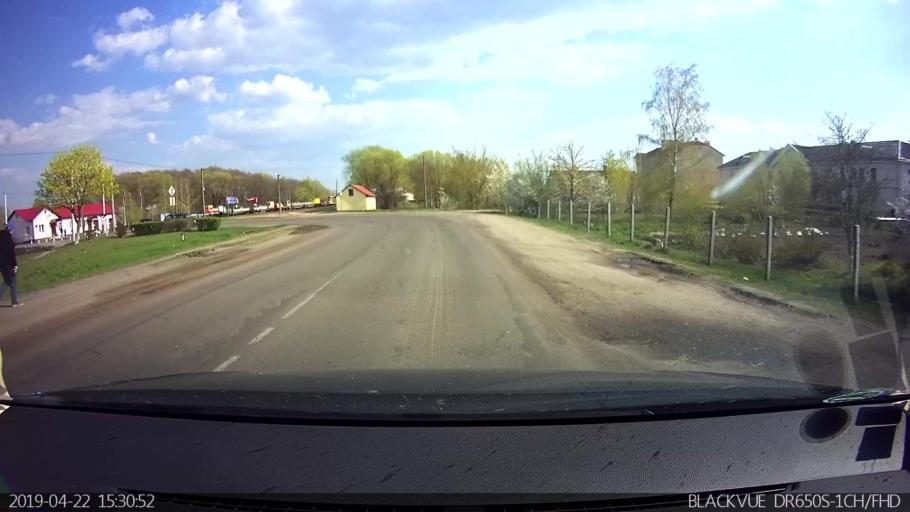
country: BY
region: Brest
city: Vysokaye
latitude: 52.3989
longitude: 23.3823
